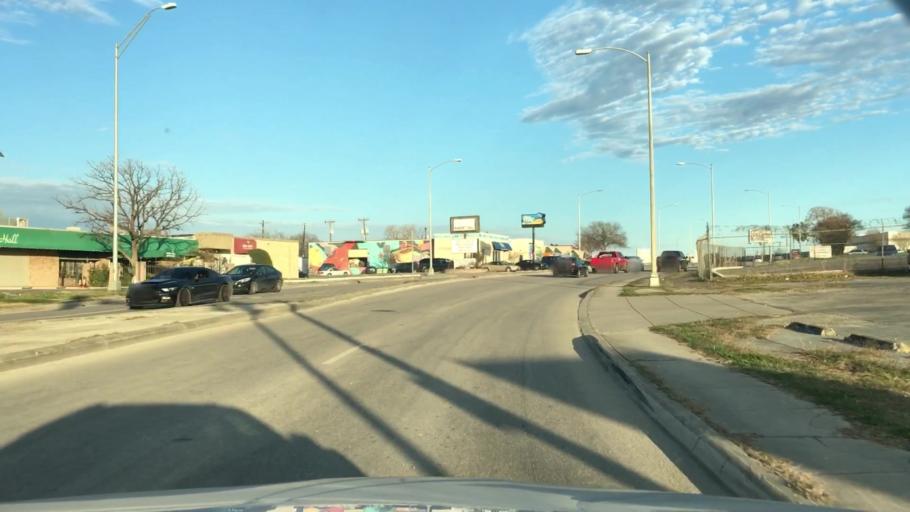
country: US
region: Texas
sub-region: Bexar County
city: Windcrest
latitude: 29.5434
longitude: -98.4178
